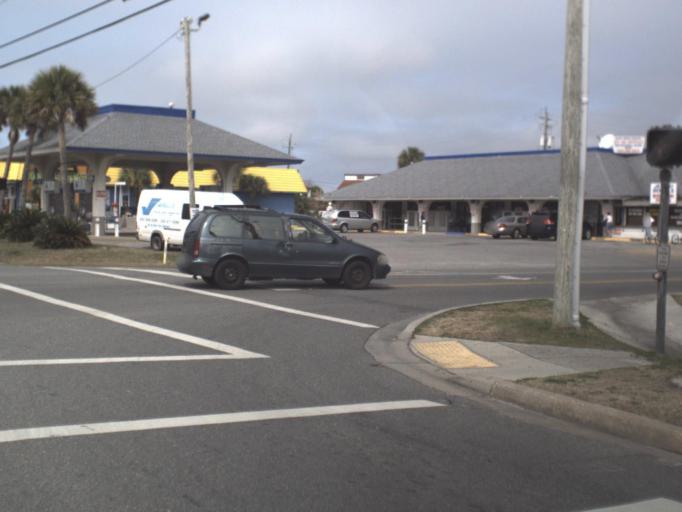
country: US
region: Florida
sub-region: Bay County
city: Panama City Beach
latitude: 30.1848
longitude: -85.8186
